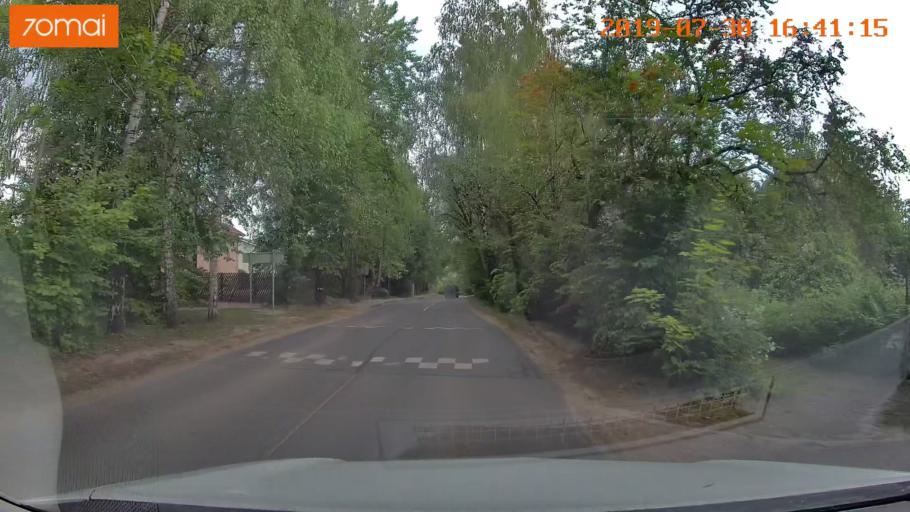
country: LT
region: Vilnius County
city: Rasos
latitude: 54.7100
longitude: 25.3574
